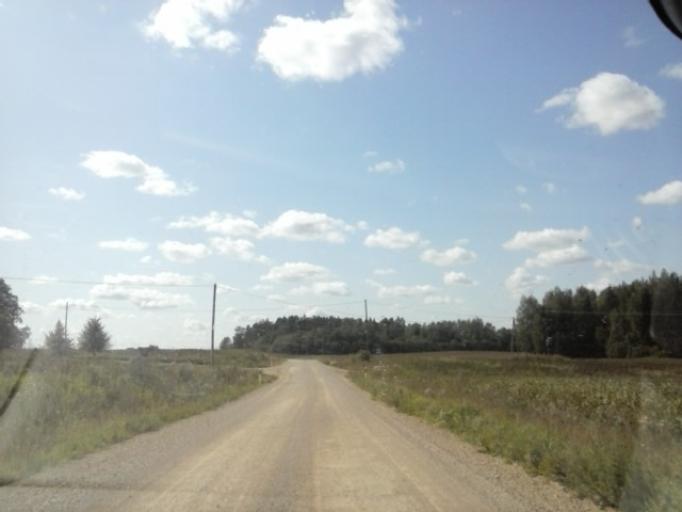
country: EE
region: Polvamaa
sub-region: Polva linn
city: Polva
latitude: 58.1067
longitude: 26.8600
